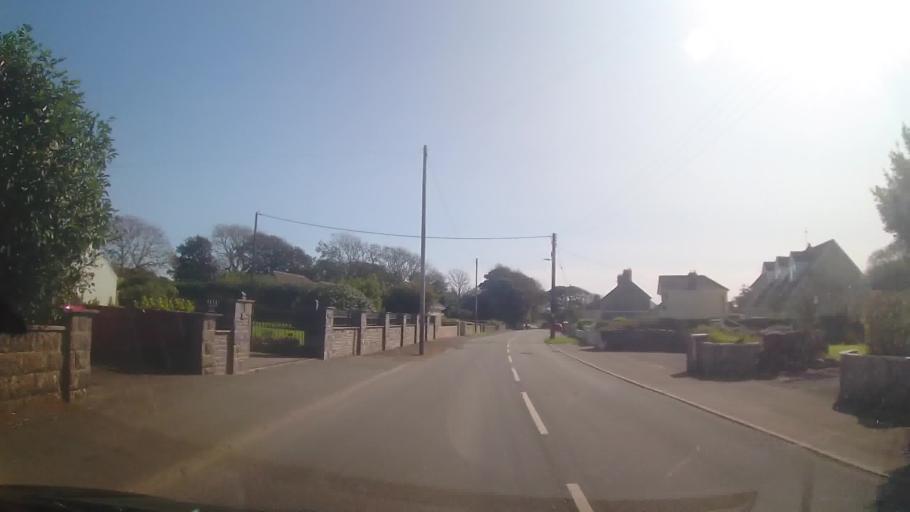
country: GB
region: Wales
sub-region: Pembrokeshire
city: Scleddau
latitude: 51.9297
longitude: -5.0063
